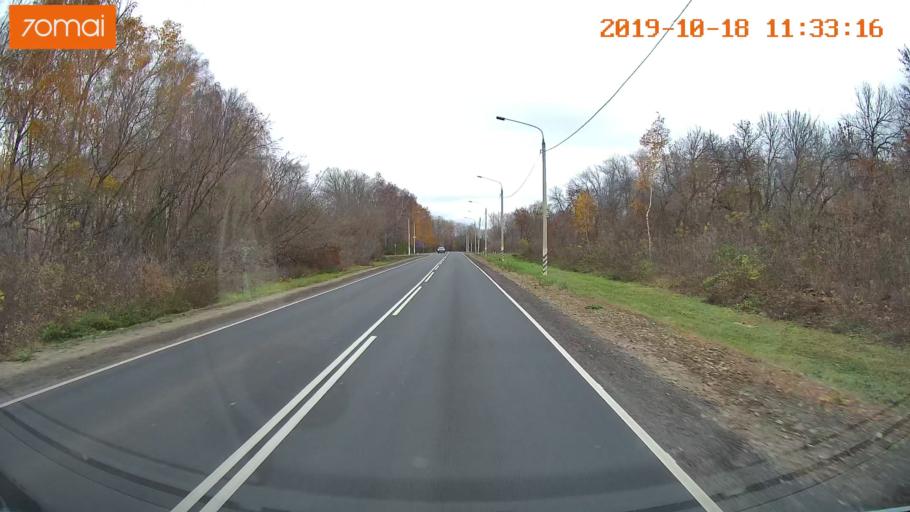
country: RU
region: Rjazan
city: Oktyabr'skiy
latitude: 54.1416
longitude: 38.7361
